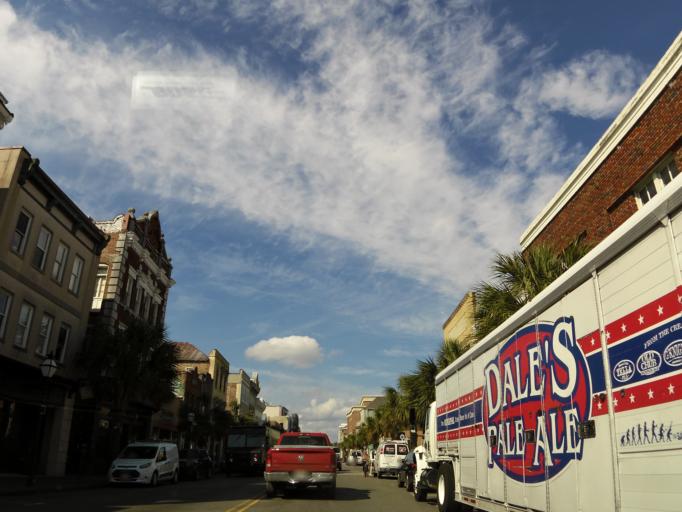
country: US
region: South Carolina
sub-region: Charleston County
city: Charleston
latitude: 32.7912
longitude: -79.9399
